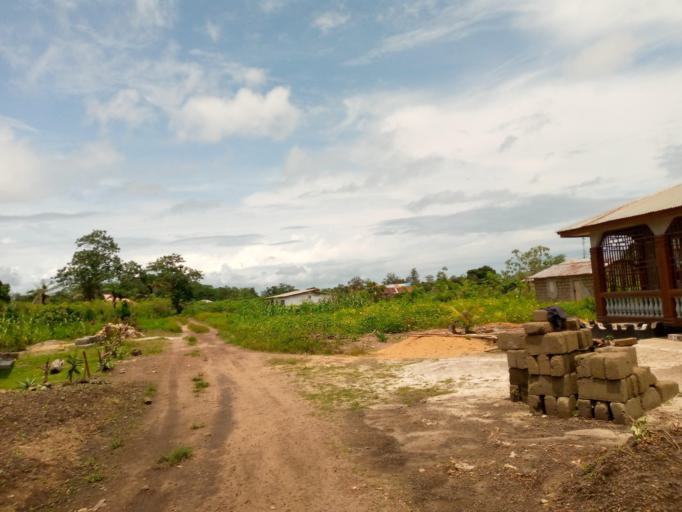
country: SL
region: Northern Province
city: Magburaka
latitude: 8.7293
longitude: -11.9287
